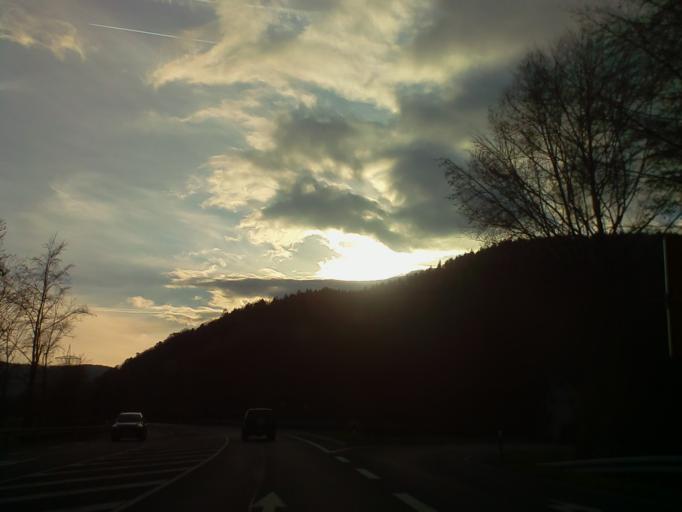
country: DE
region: Bavaria
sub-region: Regierungsbezirk Unterfranken
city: Weilbach
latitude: 49.6693
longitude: 9.2108
